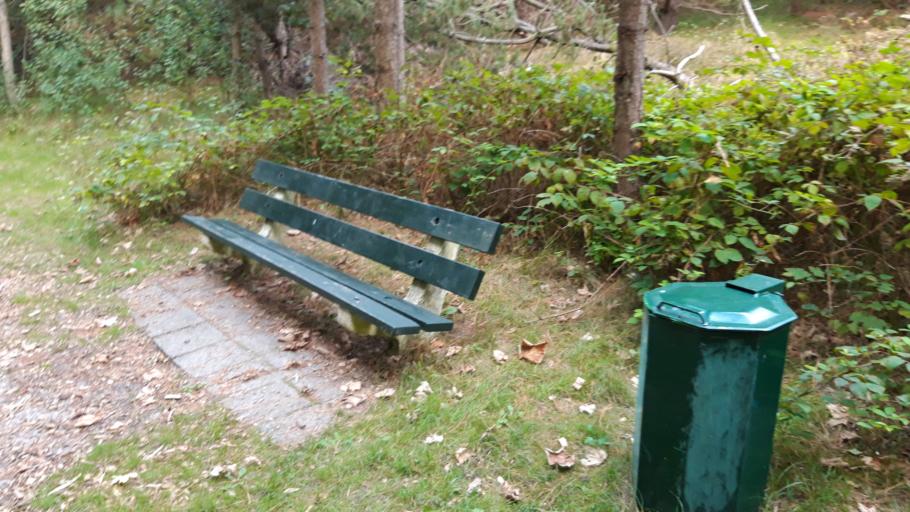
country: NL
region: Friesland
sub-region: Gemeente Ameland
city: Nes
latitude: 53.4554
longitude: 5.7657
